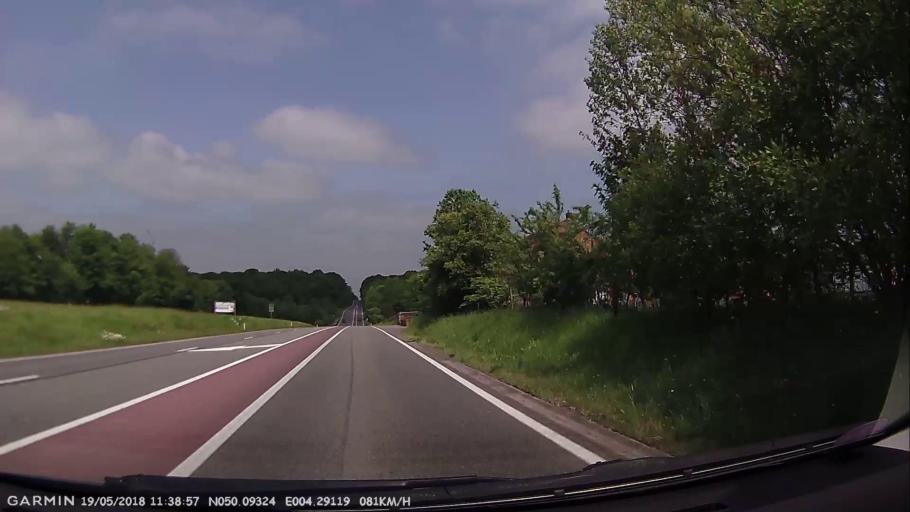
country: BE
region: Wallonia
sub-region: Province du Hainaut
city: Chimay
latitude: 50.0935
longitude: 4.2911
